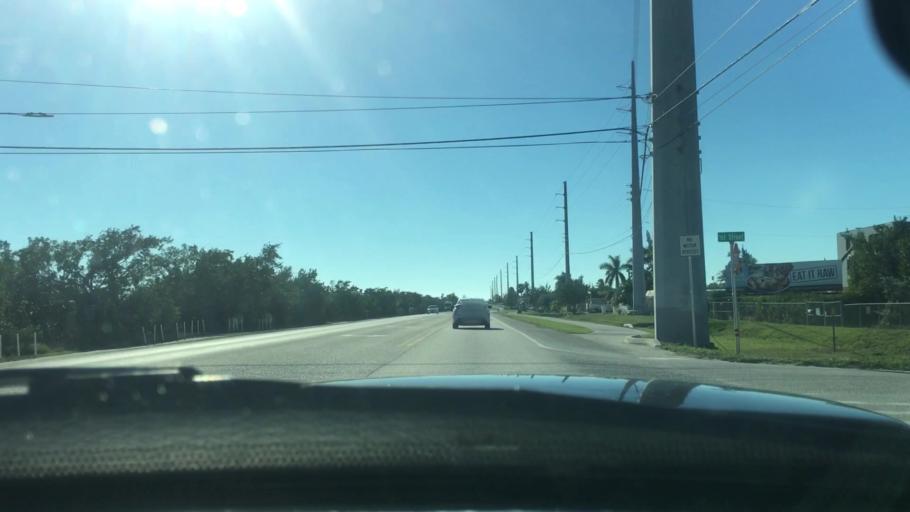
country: US
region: Florida
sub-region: Monroe County
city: Big Coppitt Key
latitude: 24.5959
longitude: -81.6594
